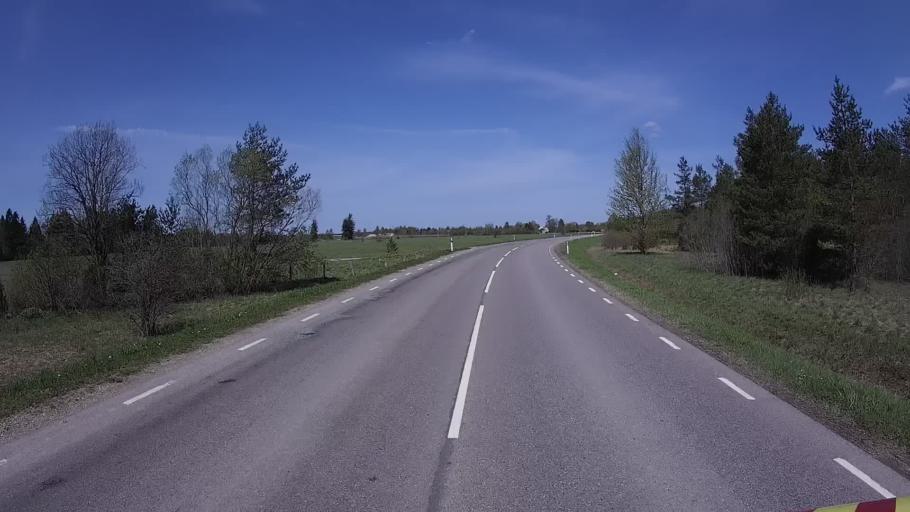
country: EE
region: Harju
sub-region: Keila linn
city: Keila
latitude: 59.2999
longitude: 24.3239
